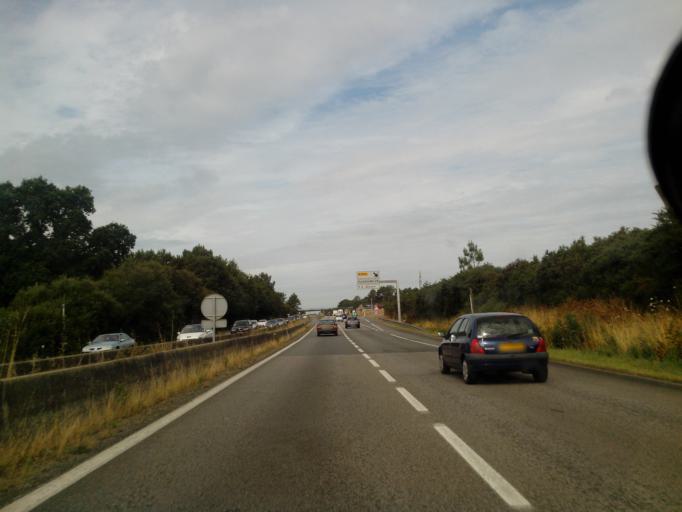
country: FR
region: Brittany
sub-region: Departement du Morbihan
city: Plougoumelen
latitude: 47.6640
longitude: -2.8924
